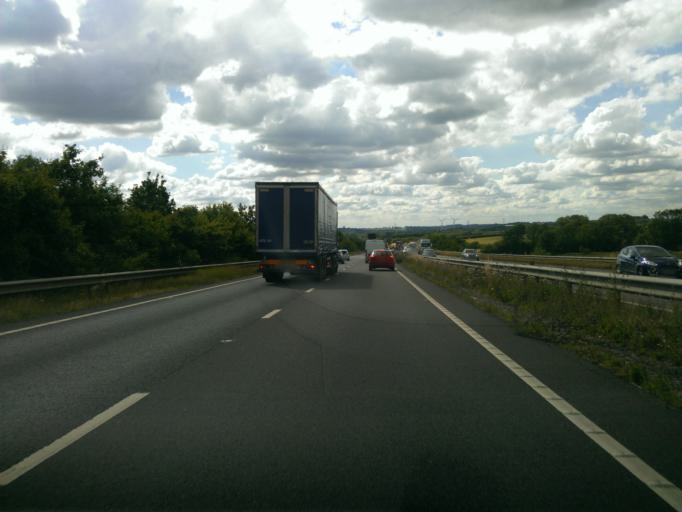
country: GB
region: England
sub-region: Northamptonshire
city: Long Buckby
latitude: 52.3925
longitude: -1.0875
